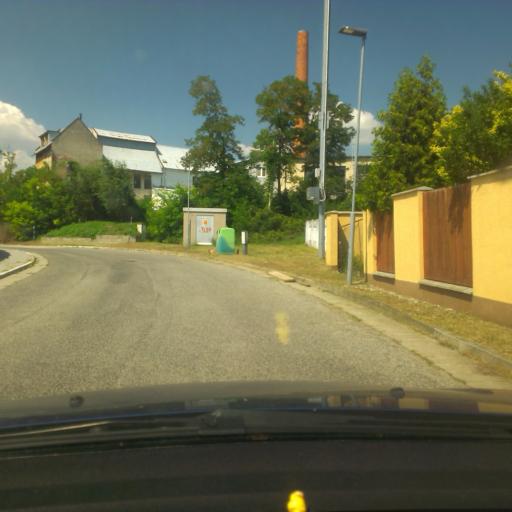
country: SK
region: Trnavsky
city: Hlohovec
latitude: 48.4432
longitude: 17.8131
